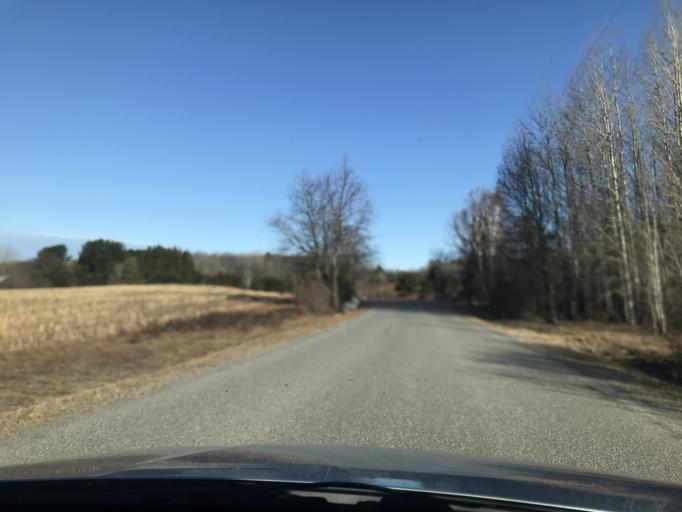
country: US
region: Wisconsin
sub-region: Marinette County
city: Niagara
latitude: 45.3842
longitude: -88.0411
